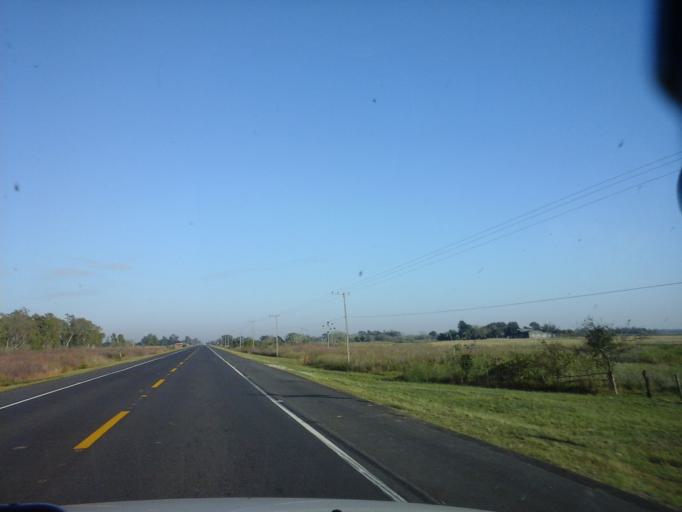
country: PY
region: Neembucu
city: Pilar
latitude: -26.8579
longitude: -58.0093
